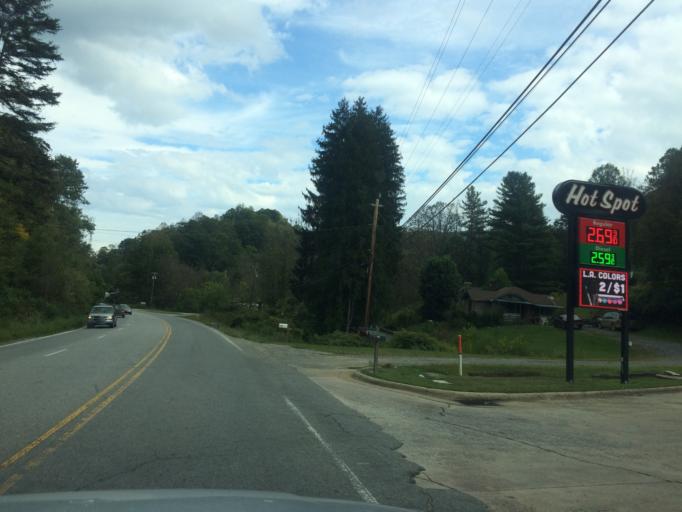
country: US
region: North Carolina
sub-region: Haywood County
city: Canton
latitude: 35.5343
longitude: -82.8228
